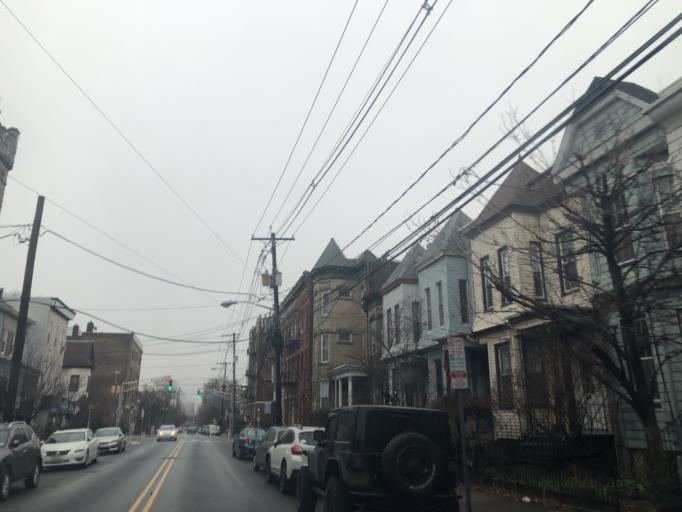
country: US
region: New Jersey
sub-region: Hudson County
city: Hoboken
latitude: 40.7465
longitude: -74.0521
